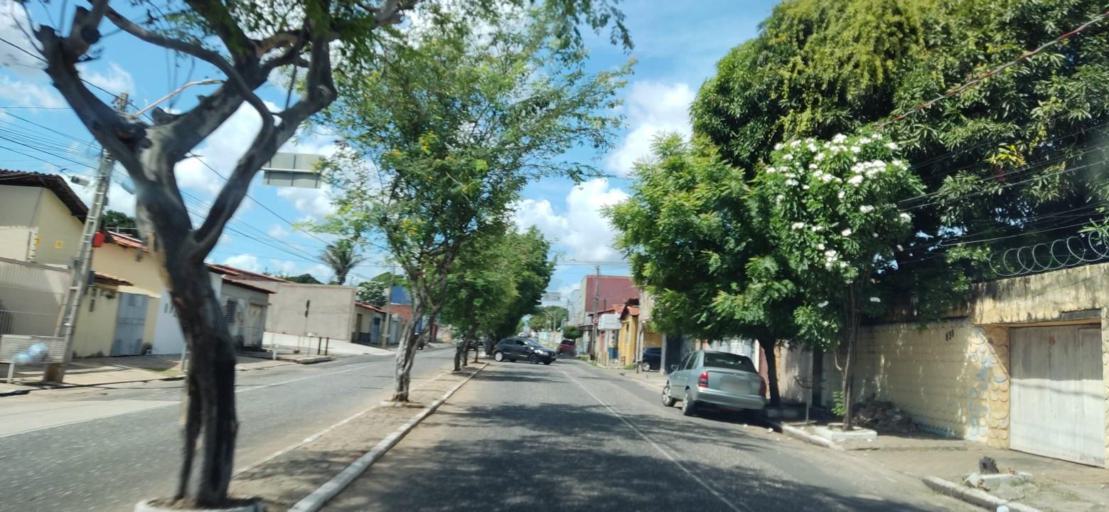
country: BR
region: Maranhao
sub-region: Timon
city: Timon
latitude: -5.0812
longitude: -42.8253
